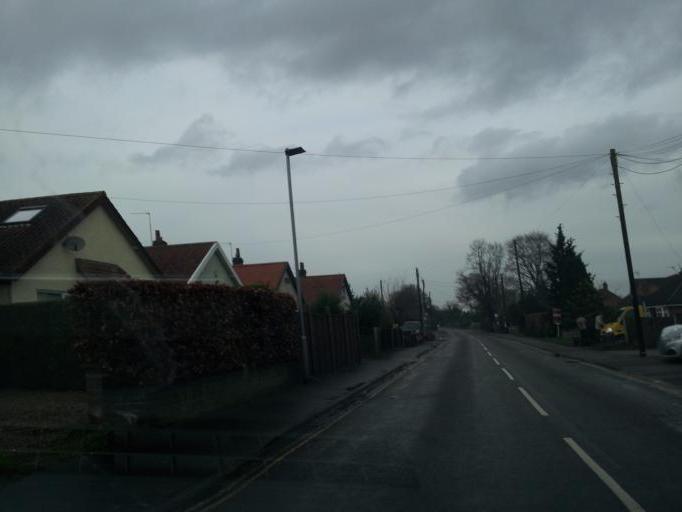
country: GB
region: England
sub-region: Norfolk
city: Brundall
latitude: 52.6255
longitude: 1.4256
